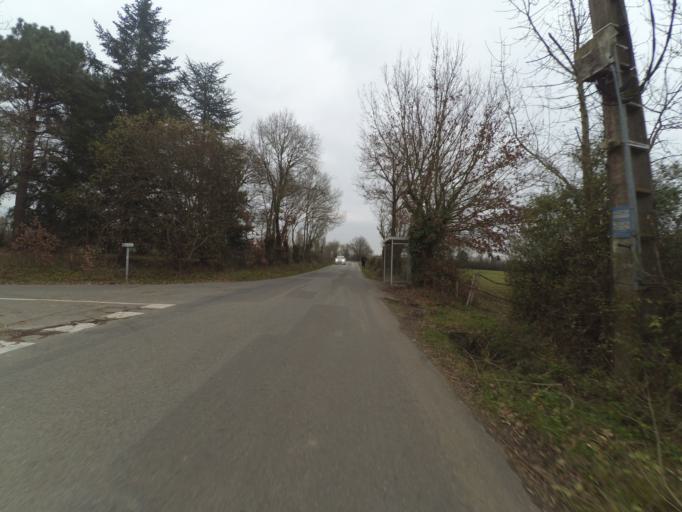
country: FR
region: Pays de la Loire
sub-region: Departement de la Loire-Atlantique
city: Indre
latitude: 47.2300
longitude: -1.6876
